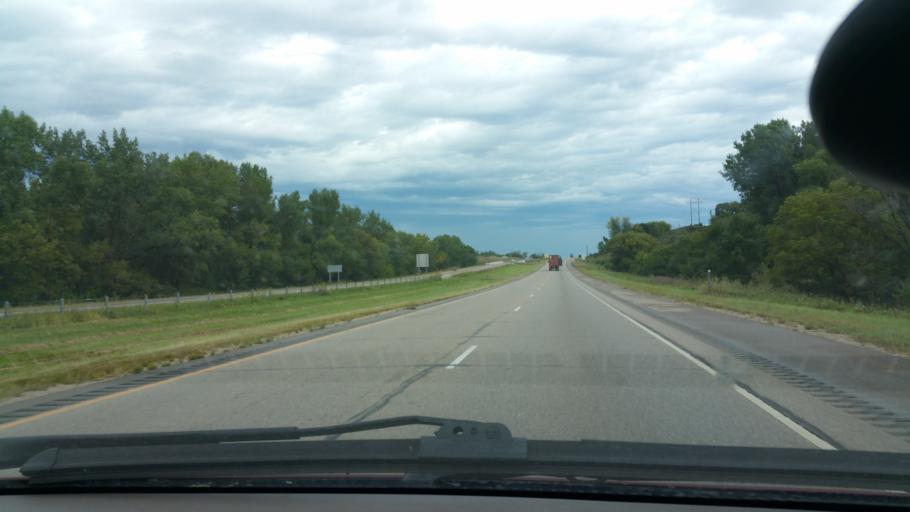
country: US
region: Minnesota
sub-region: Rice County
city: Faribault
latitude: 44.2964
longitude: -93.3091
